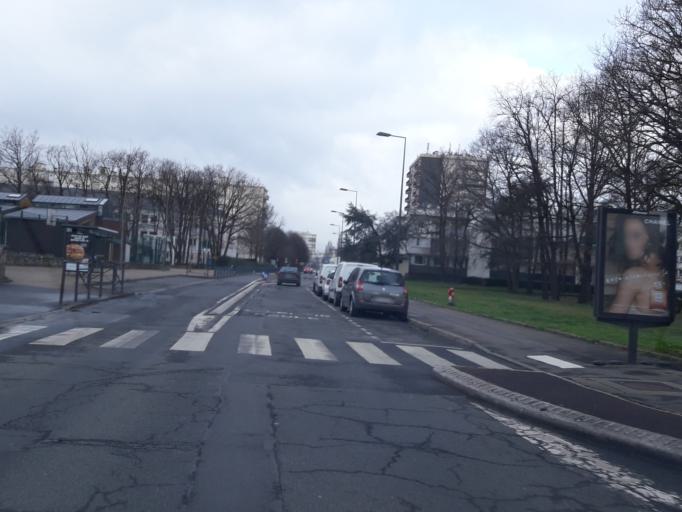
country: FR
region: Ile-de-France
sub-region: Departement de l'Essonne
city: Sainte-Genevieve-des-Bois
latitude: 48.6322
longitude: 2.3260
